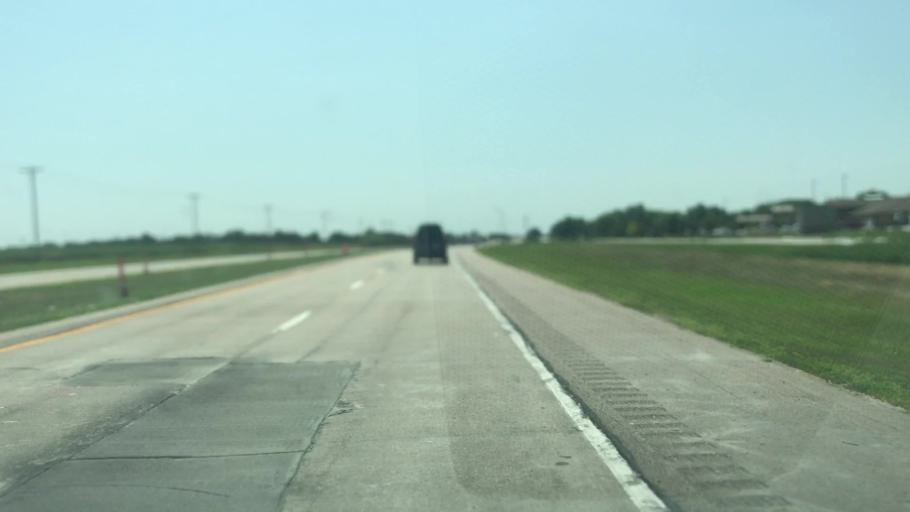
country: US
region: Nebraska
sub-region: Adams County
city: Hastings
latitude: 40.6440
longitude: -98.3822
